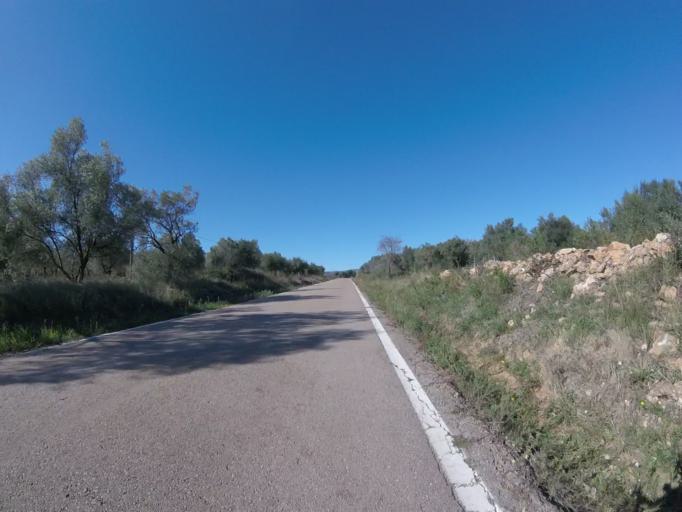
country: ES
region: Valencia
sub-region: Provincia de Castello
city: Chert/Xert
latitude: 40.4537
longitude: 0.1308
